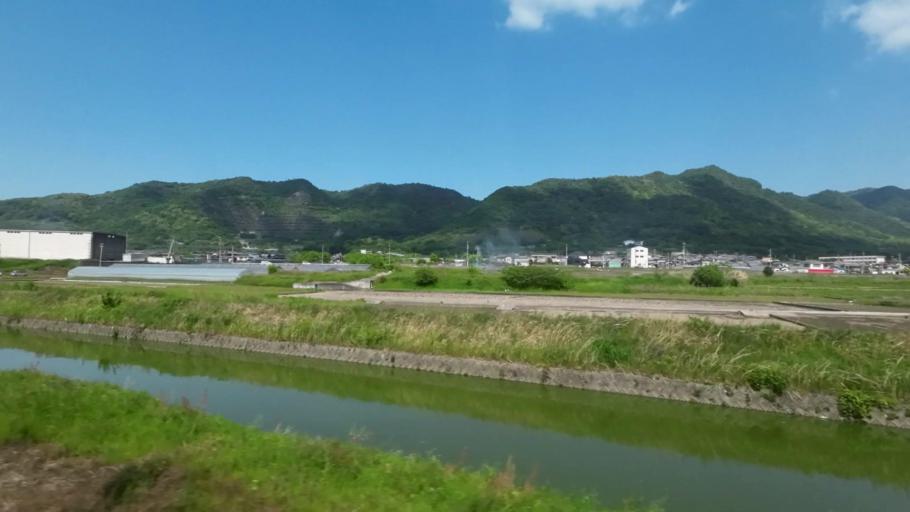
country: JP
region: Kagawa
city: Kan'onjicho
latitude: 34.1491
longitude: 133.6869
